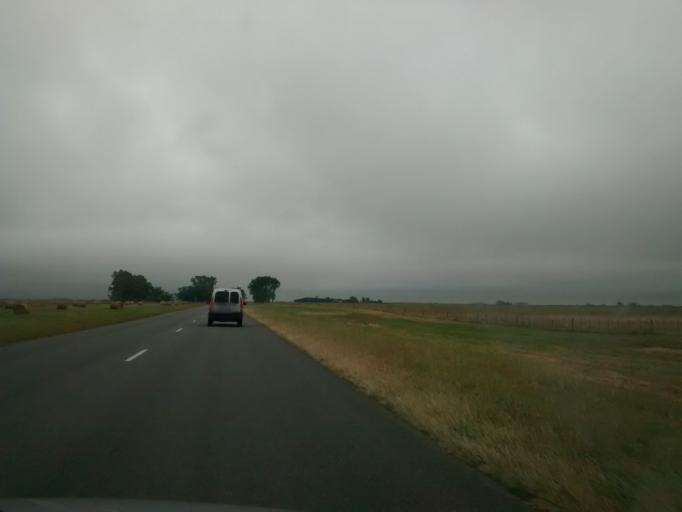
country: AR
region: Buenos Aires
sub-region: Partido de Ayacucho
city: Ayacucho
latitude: -37.2453
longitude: -58.4885
